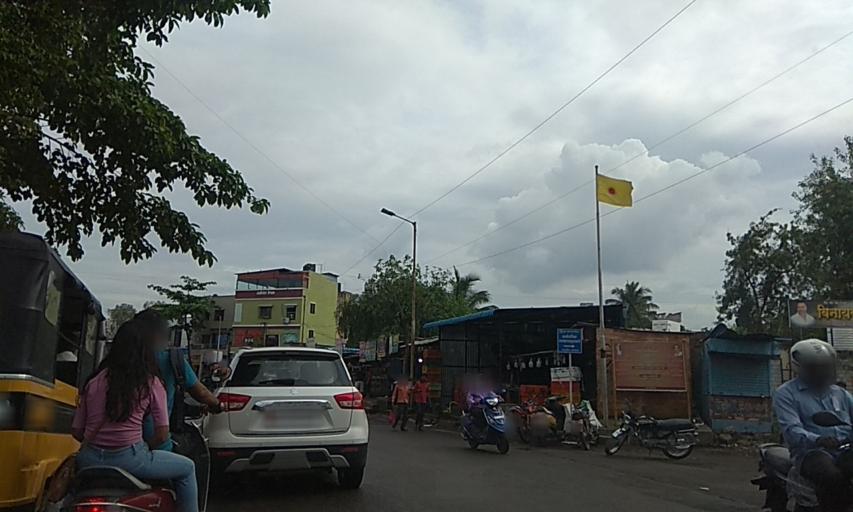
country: IN
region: Maharashtra
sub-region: Pune Division
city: Lohogaon
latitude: 18.5585
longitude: 73.9314
